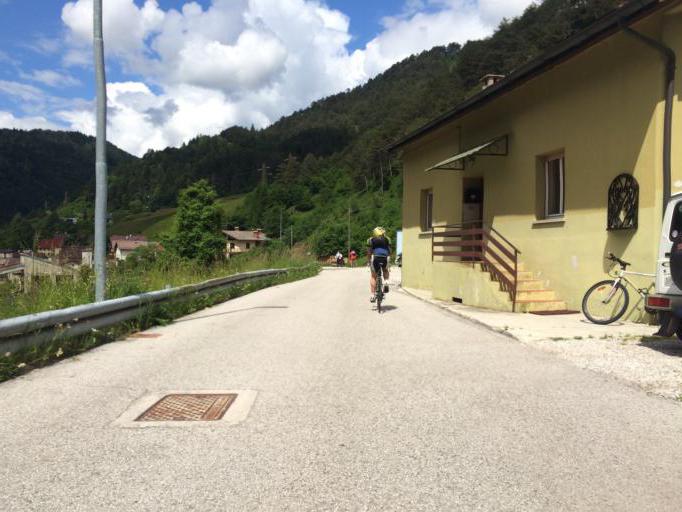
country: IT
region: Friuli Venezia Giulia
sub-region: Provincia di Udine
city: Pontebba
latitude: 46.5105
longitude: 13.3181
